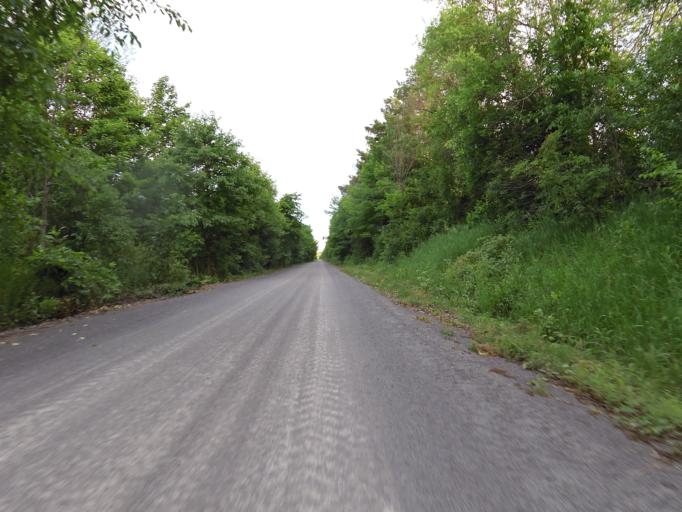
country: CA
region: Ontario
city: Arnprior
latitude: 45.3391
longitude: -76.2973
